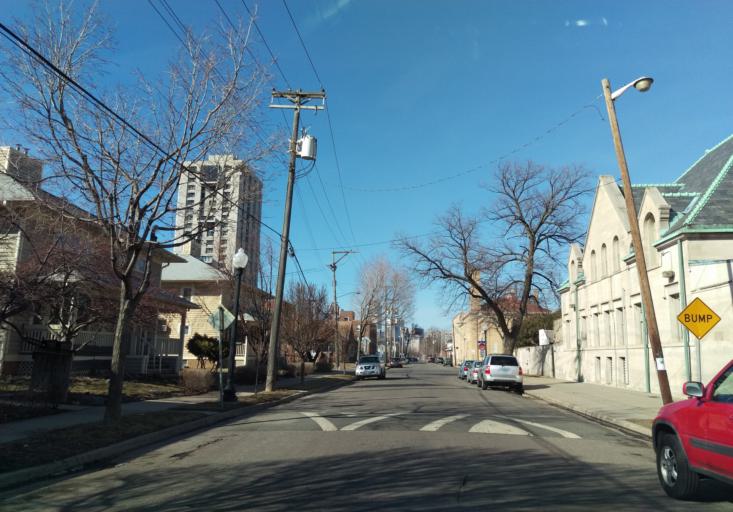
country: US
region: Minnesota
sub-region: Hennepin County
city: Minneapolis
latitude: 44.9549
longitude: -93.2664
